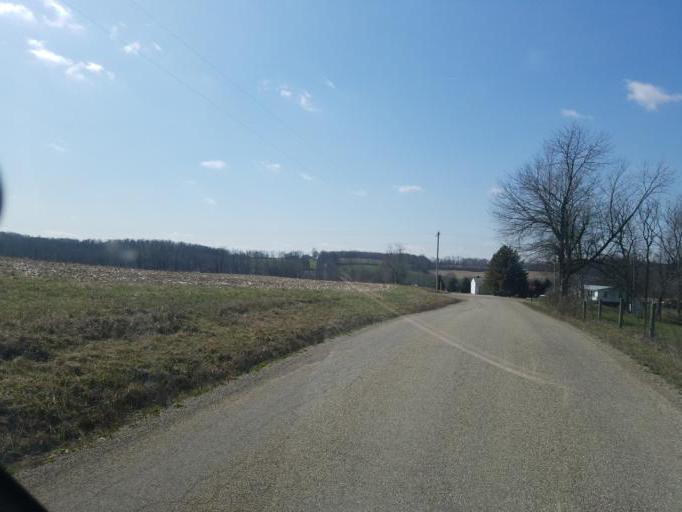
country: US
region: Ohio
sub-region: Licking County
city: Utica
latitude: 40.2481
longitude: -82.3379
